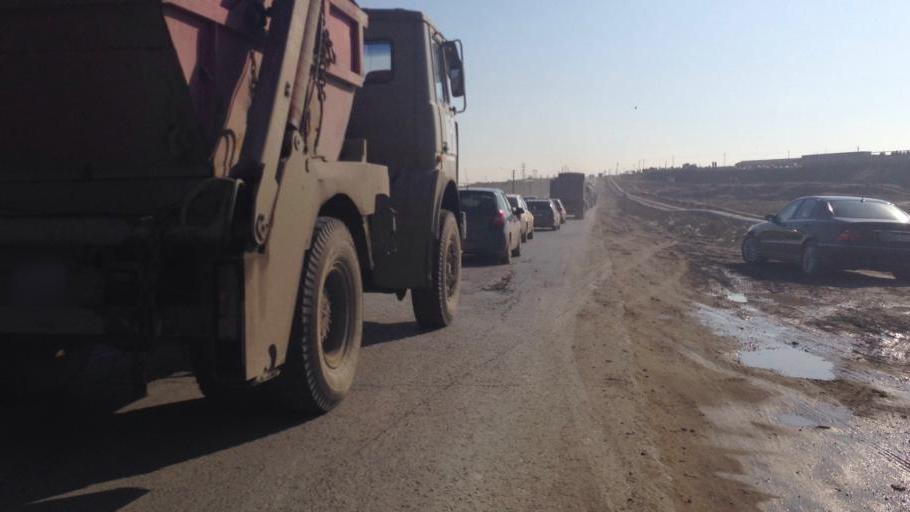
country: AZ
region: Abseron
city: Digah
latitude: 40.4678
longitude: 49.8863
